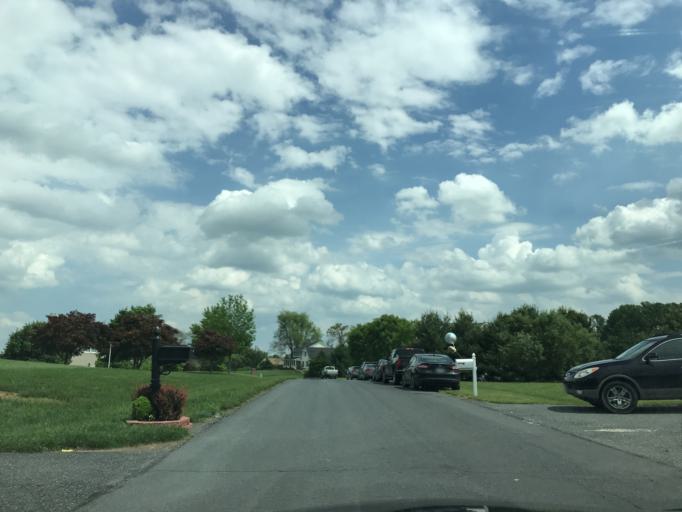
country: US
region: Maryland
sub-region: Harford County
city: Bel Air North
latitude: 39.5983
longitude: -76.3493
